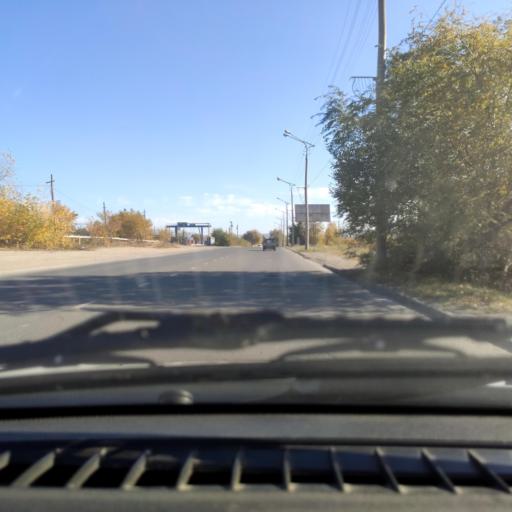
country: RU
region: Samara
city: Zhigulevsk
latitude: 53.4758
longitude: 49.5291
